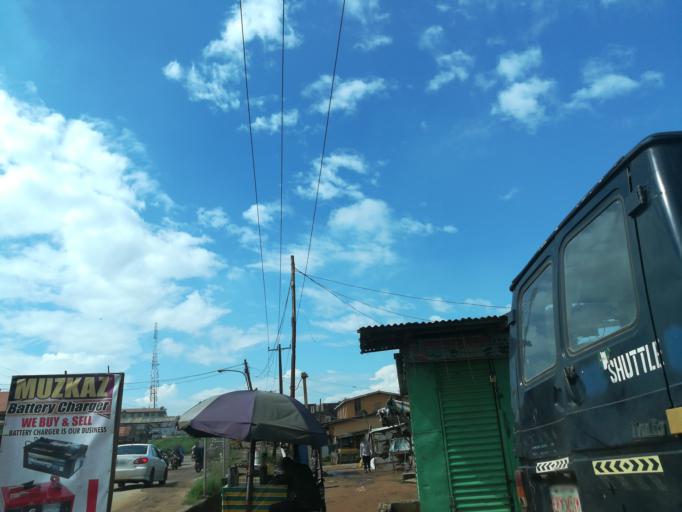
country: NG
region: Lagos
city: Ikorodu
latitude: 6.6009
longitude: 3.5184
